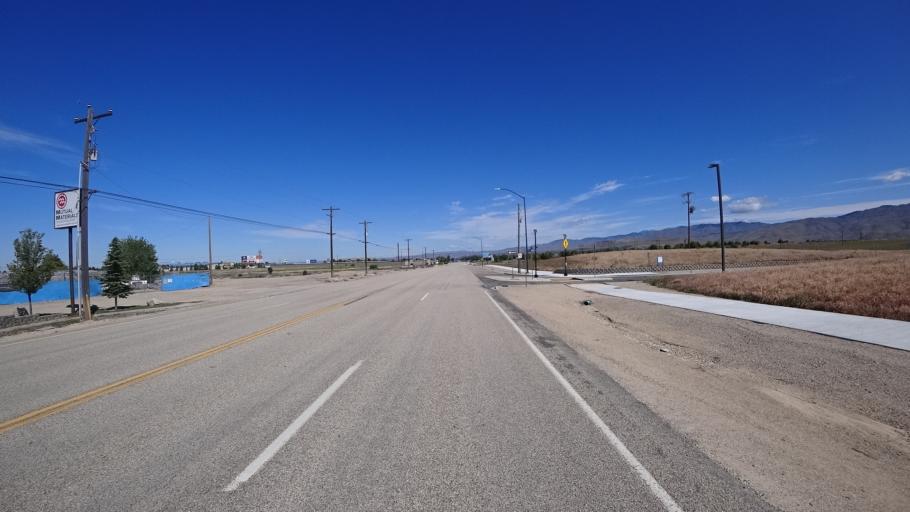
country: US
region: Idaho
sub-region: Ada County
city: Boise
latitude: 43.5348
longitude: -116.1530
